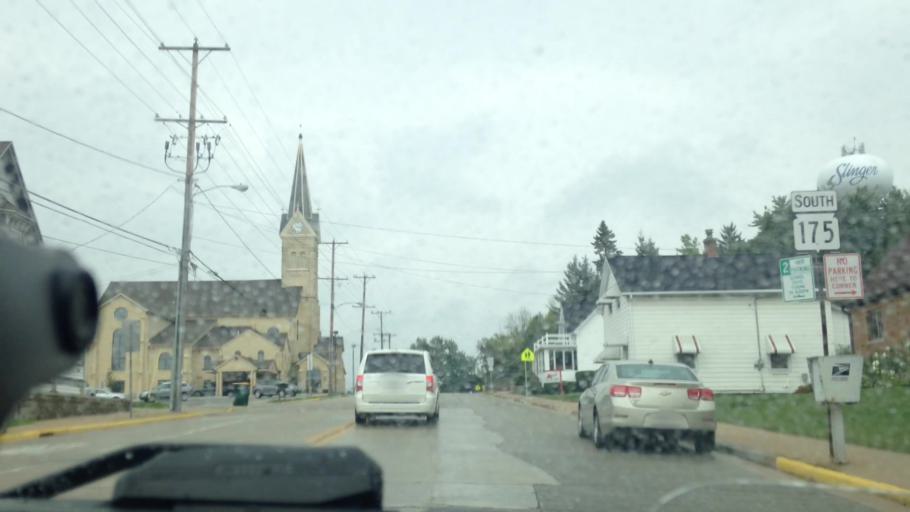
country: US
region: Wisconsin
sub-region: Washington County
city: Slinger
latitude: 43.3343
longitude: -88.2851
